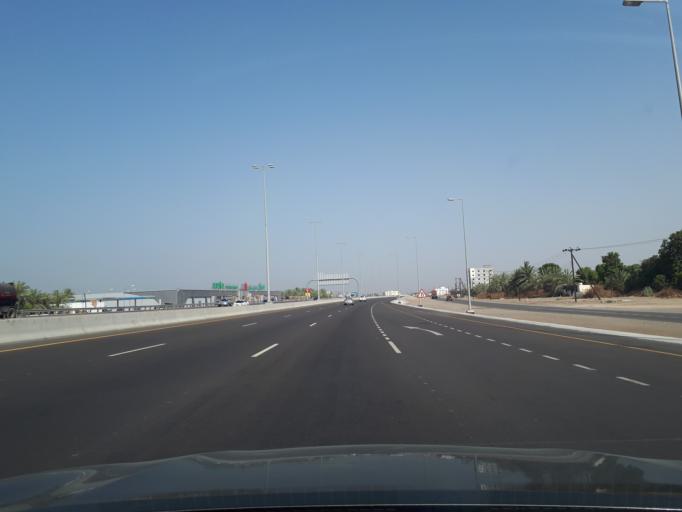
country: OM
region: Al Batinah
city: Al Liwa'
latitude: 24.4183
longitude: 56.6256
